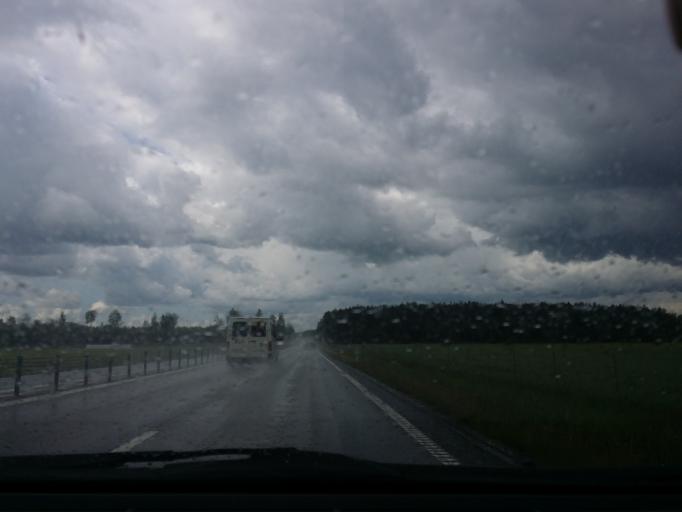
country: SE
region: Vaestmanland
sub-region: Hallstahammars Kommun
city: Hallstahammar
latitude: 59.5846
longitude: 16.1842
